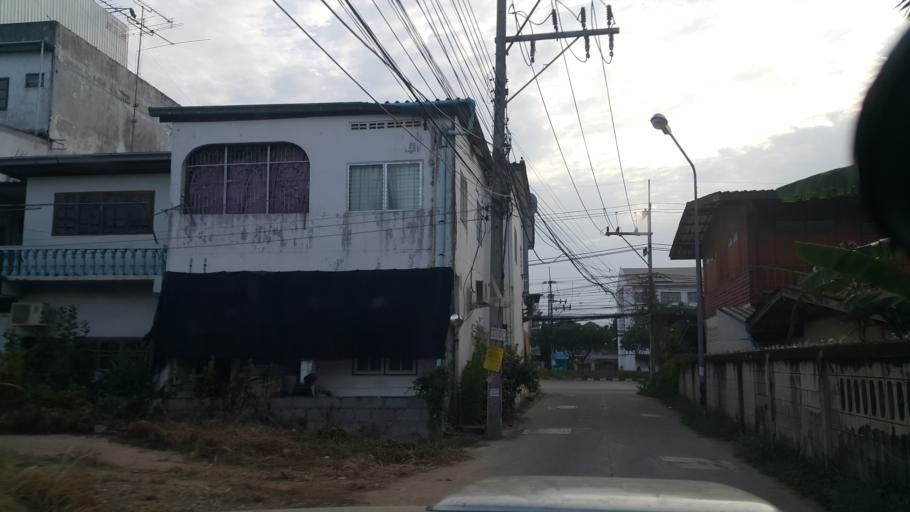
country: TH
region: Chon Buri
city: Phatthaya
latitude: 12.8181
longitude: 100.9172
